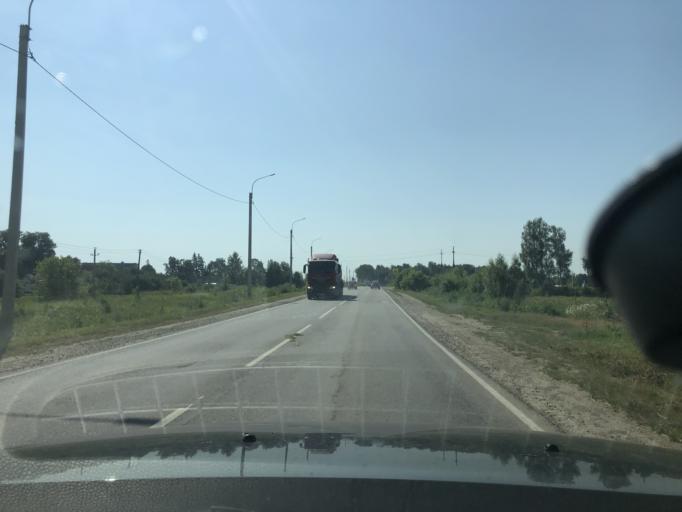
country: RU
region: Tula
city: Dubna
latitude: 54.1082
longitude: 37.1054
